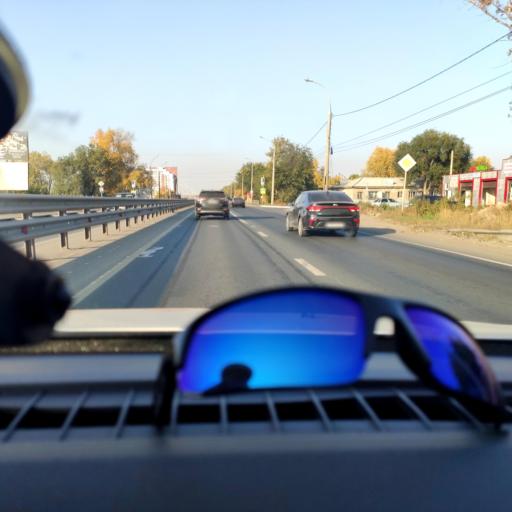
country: RU
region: Samara
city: Samara
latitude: 53.1106
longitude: 50.1650
